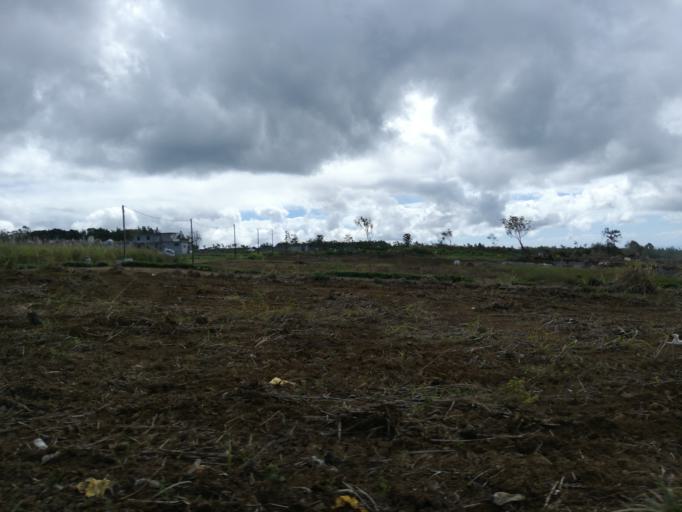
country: MU
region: Moka
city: Camp Thorel
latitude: -20.2125
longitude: 57.5964
